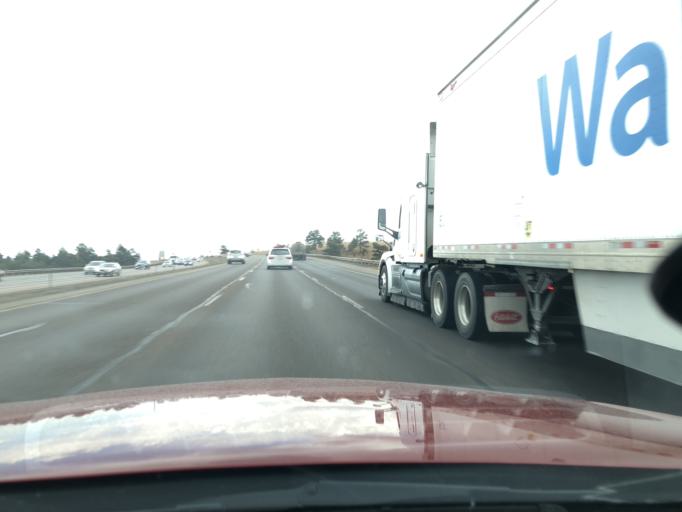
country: US
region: Colorado
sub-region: Jefferson County
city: Genesee
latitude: 39.7070
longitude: -105.2790
